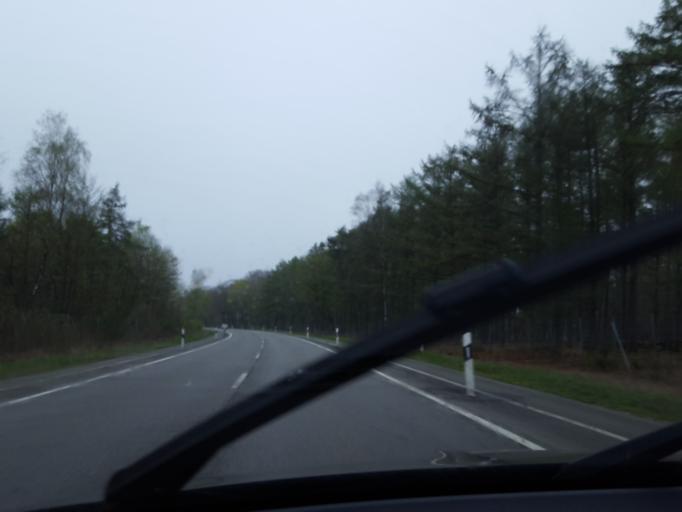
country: DE
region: North Rhine-Westphalia
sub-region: Regierungsbezirk Dusseldorf
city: Schermbeck
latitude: 51.7203
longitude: 6.9215
